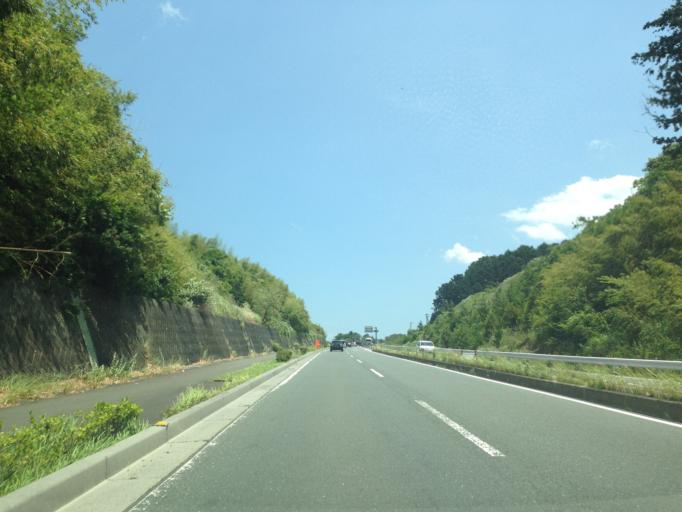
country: JP
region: Shizuoka
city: Kakegawa
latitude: 34.7536
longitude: 137.9967
